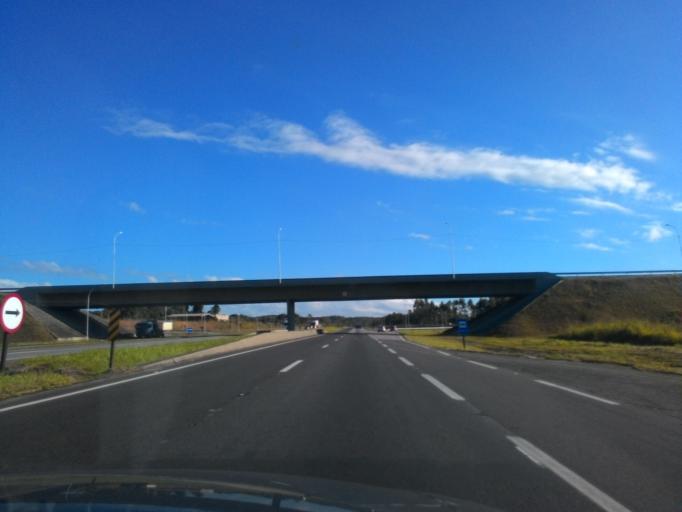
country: BR
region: Sao Paulo
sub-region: Pariquera-Acu
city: Pariquera Acu
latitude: -24.6435
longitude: -47.9180
